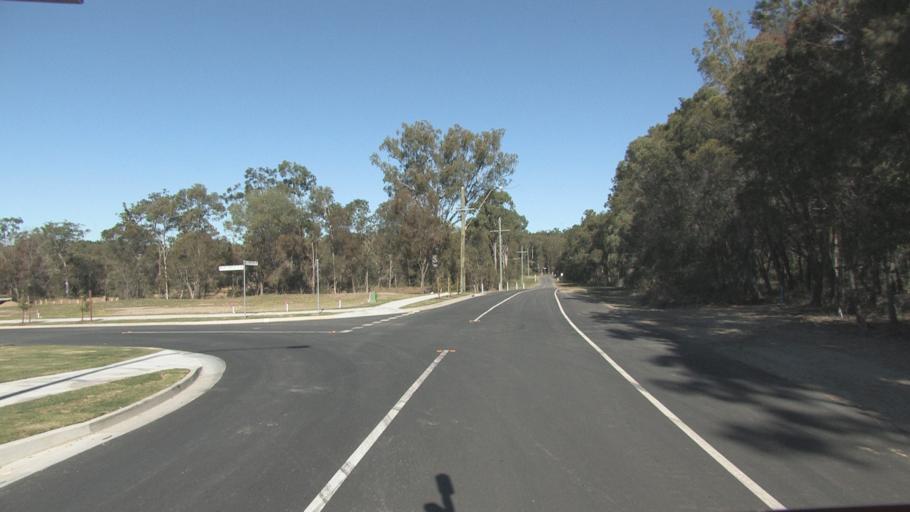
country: AU
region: Queensland
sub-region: Logan
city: Logan Reserve
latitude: -27.7137
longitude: 153.0766
